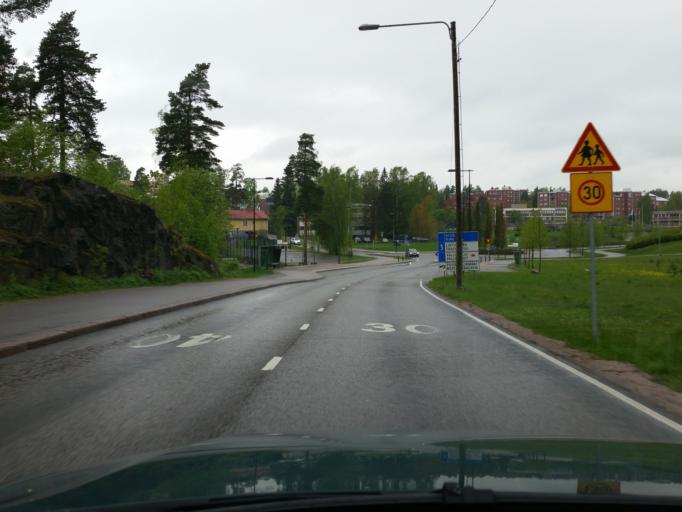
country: FI
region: Uusimaa
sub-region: Helsinki
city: Teekkarikylae
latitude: 60.2232
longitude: 24.8280
